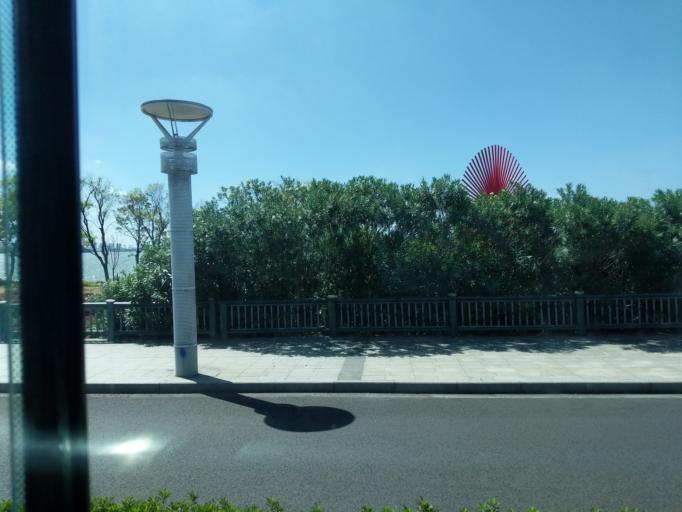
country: CN
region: Jiangsu Sheng
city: Weiting
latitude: 31.3271
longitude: 120.6873
